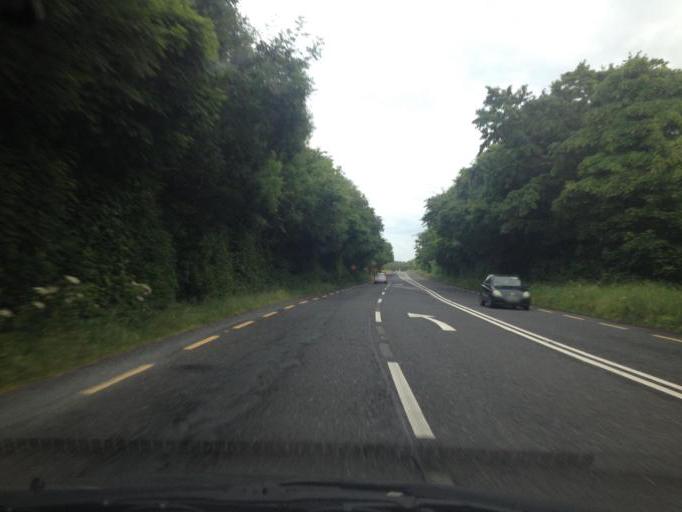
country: IE
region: Connaught
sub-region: Sligo
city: Sligo
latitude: 54.3823
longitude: -8.5288
